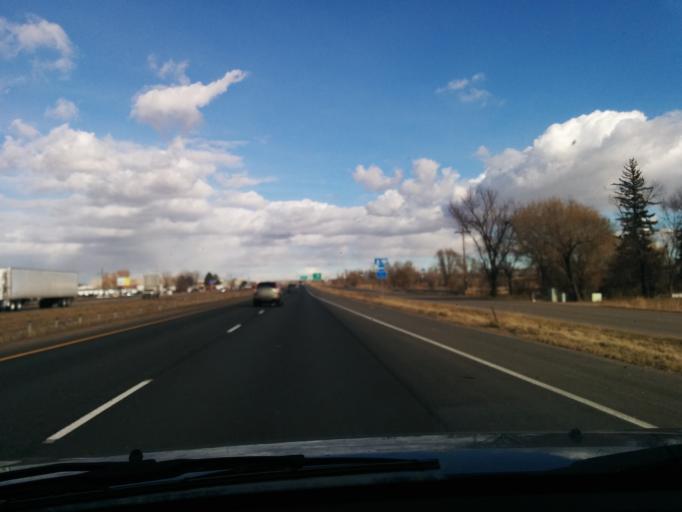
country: US
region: Colorado
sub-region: Larimer County
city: Fort Collins
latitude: 40.5720
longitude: -105.0012
